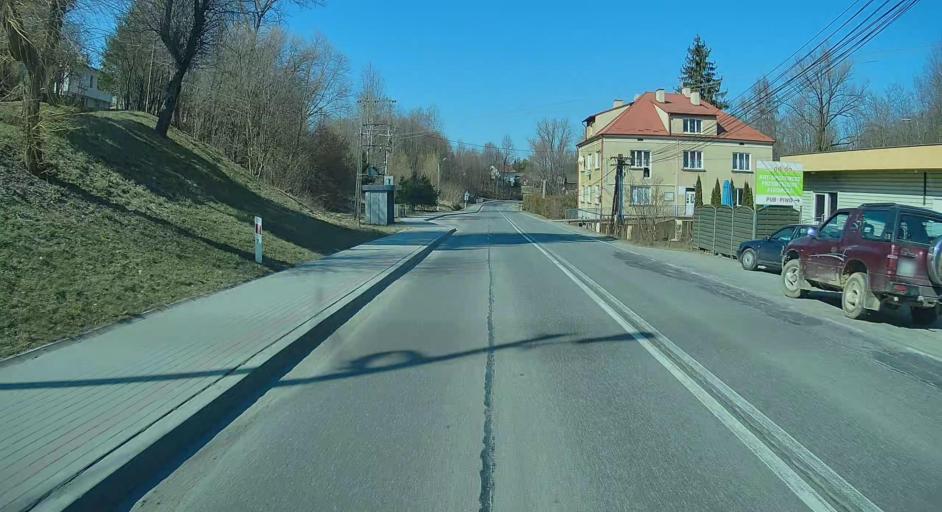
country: PL
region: Subcarpathian Voivodeship
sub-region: Powiat rzeszowski
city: Hyzne
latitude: 49.9054
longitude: 22.2069
